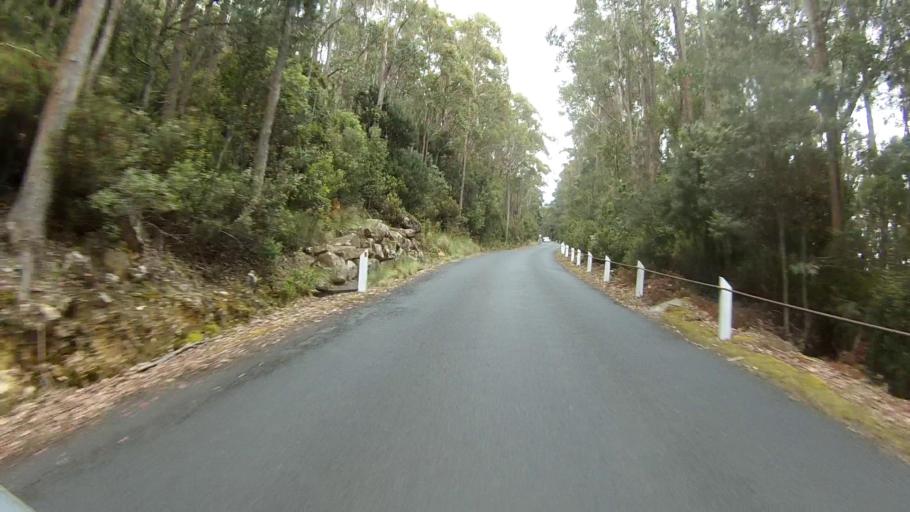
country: AU
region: Tasmania
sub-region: Glenorchy
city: West Moonah
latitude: -42.9076
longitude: 147.2440
